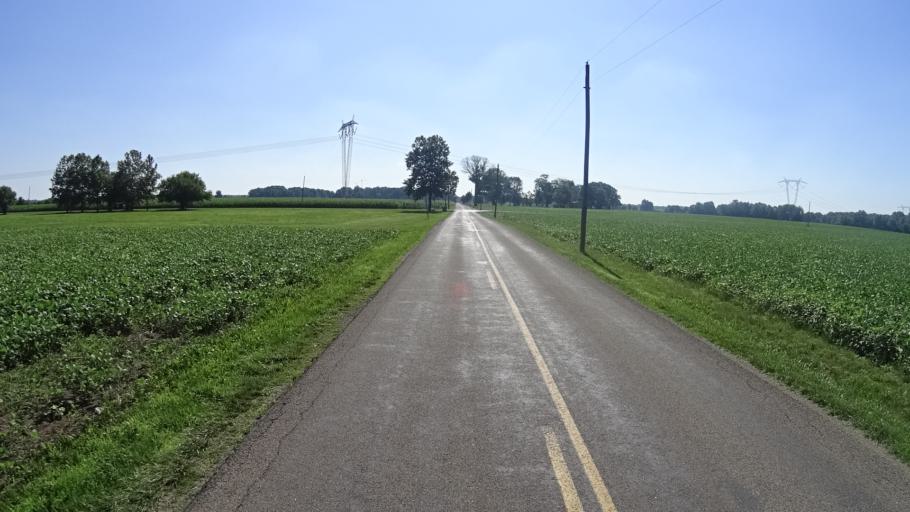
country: US
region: Indiana
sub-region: Madison County
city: Ingalls
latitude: 39.9878
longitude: -85.8164
